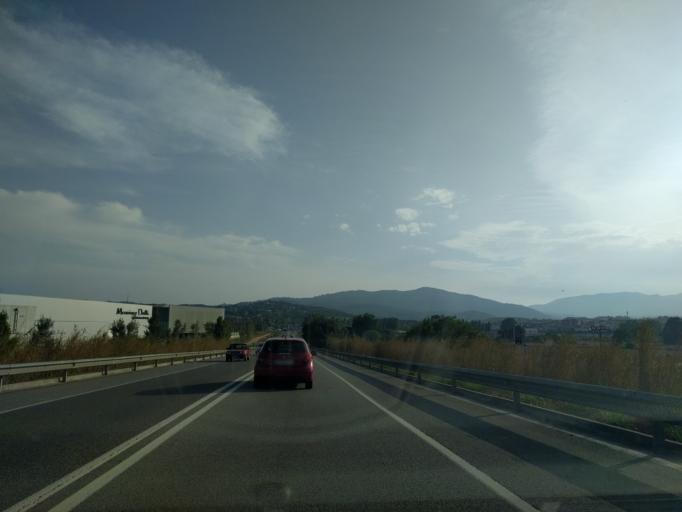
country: ES
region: Catalonia
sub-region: Provincia de Barcelona
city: Tordera
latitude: 41.6997
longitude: 2.7285
